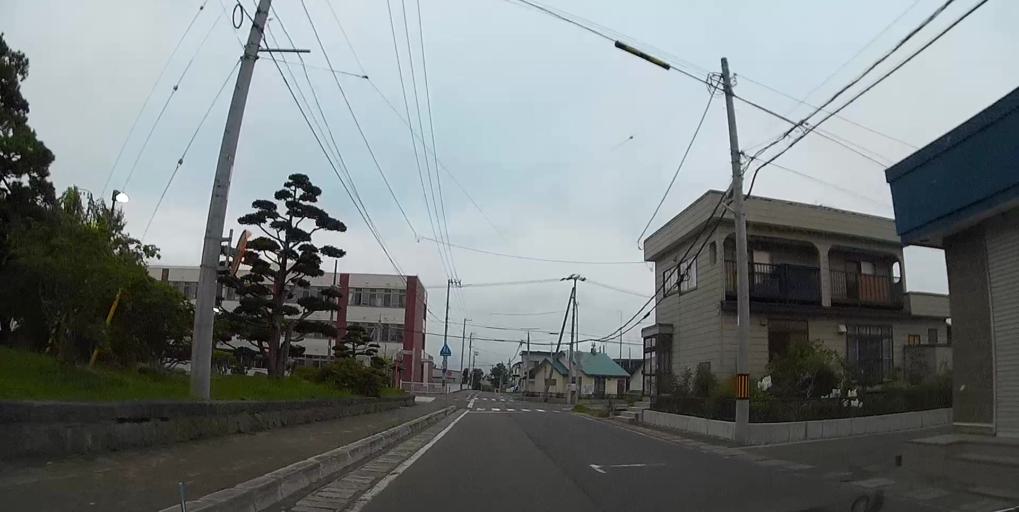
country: JP
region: Hokkaido
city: Nanae
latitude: 42.2556
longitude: 140.2661
